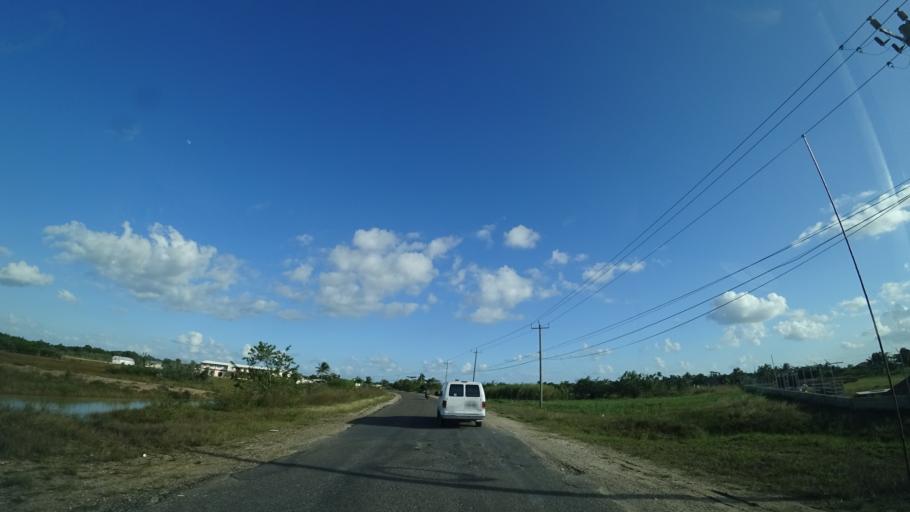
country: BZ
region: Belize
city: Belize City
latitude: 17.5580
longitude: -88.3183
